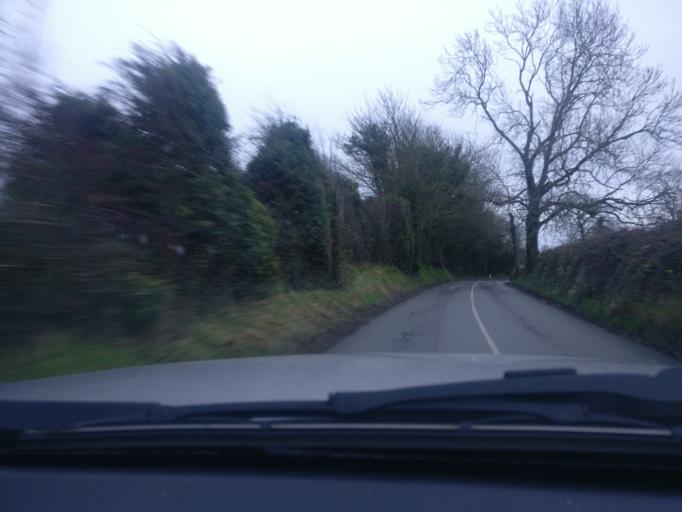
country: IE
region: Leinster
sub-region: Kildare
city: Kilcock
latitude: 53.4716
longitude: -6.6241
